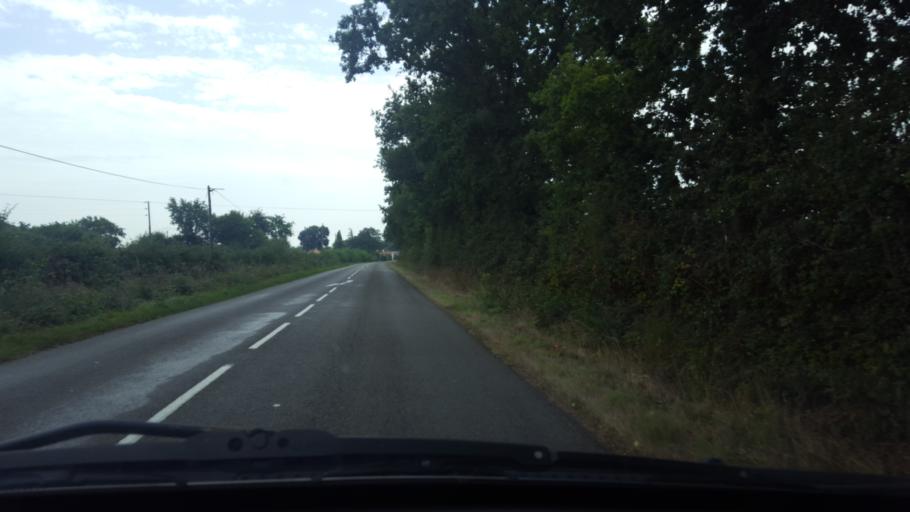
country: FR
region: Pays de la Loire
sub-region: Departement de la Loire-Atlantique
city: Touvois
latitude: 46.9152
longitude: -1.6830
